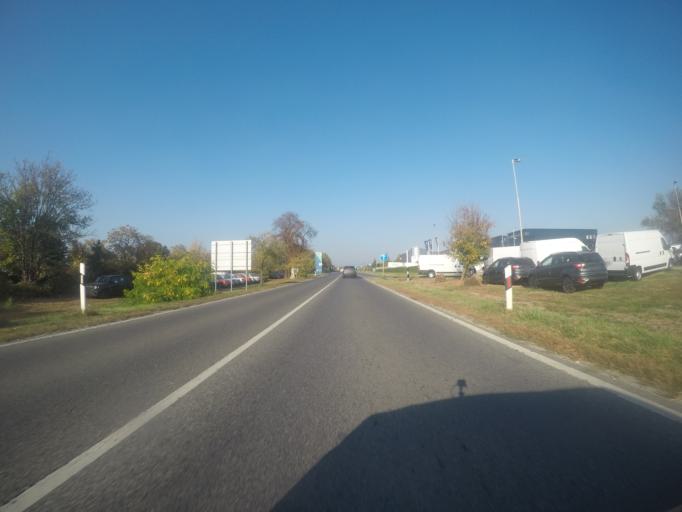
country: HU
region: Pest
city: Szazhalombatta
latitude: 47.3563
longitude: 18.9070
